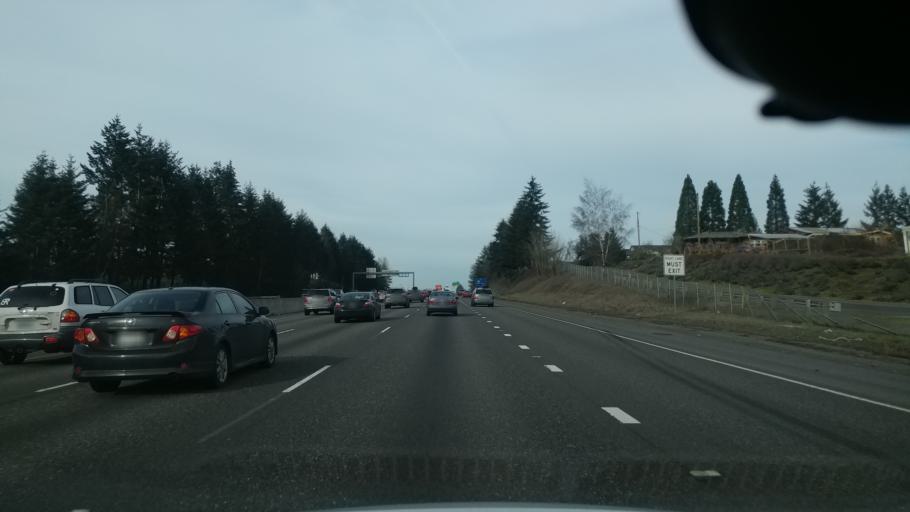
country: US
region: Washington
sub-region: Clark County
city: Mount Vista
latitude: 45.7384
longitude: -122.6588
